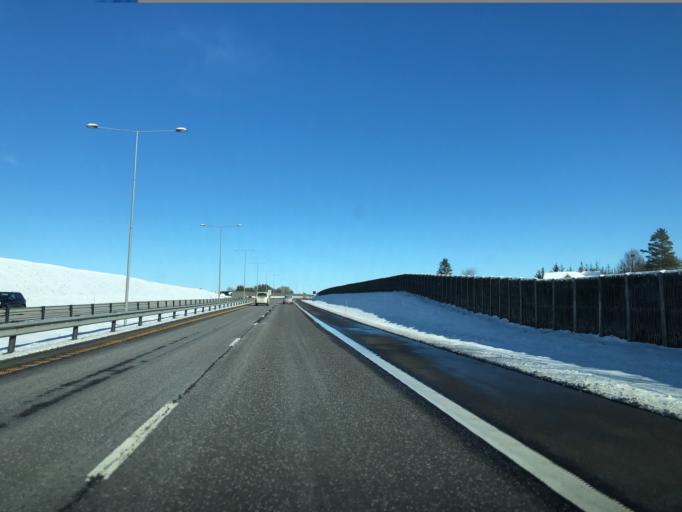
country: NO
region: Vestfold
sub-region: Sandefjord
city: Sandefjord
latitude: 59.1320
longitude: 10.1527
